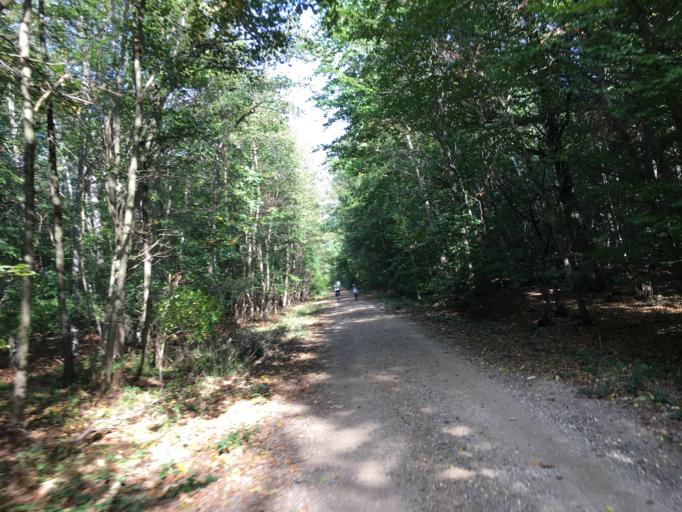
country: DE
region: North Rhine-Westphalia
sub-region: Regierungsbezirk Koln
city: Merzenich
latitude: 50.8534
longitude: 6.5356
